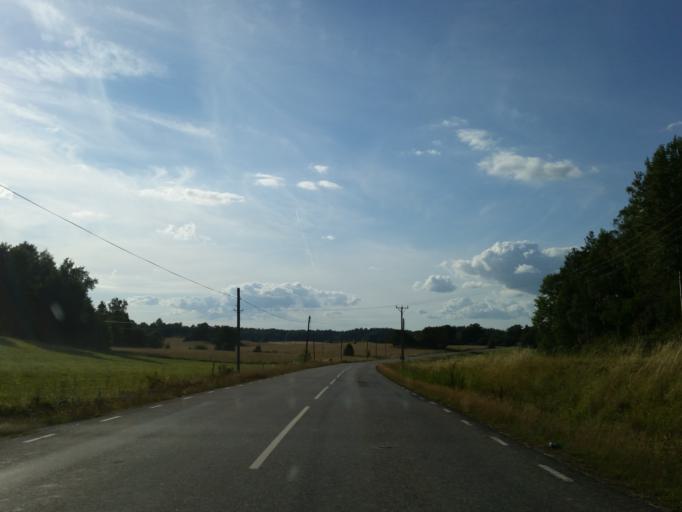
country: SE
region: Stockholm
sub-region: Sodertalje Kommun
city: Molnbo
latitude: 58.9932
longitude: 17.4159
